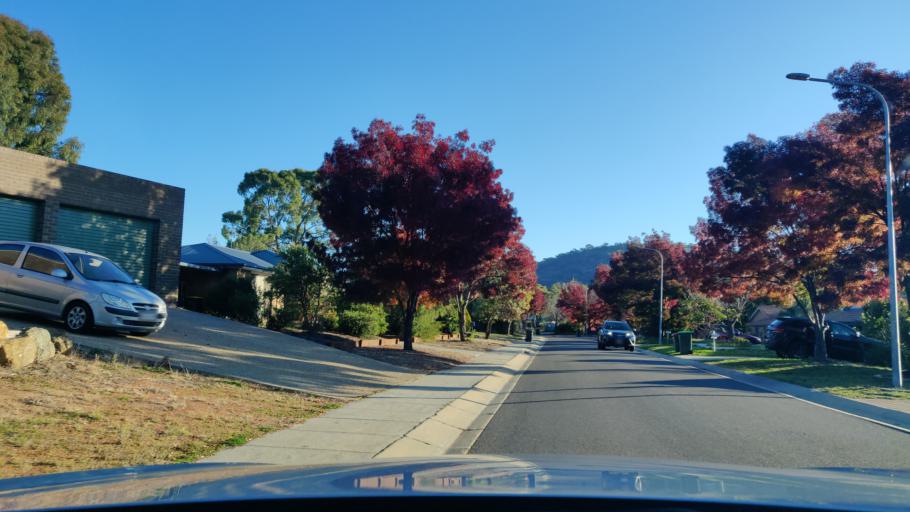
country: AU
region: Australian Capital Territory
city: Macarthur
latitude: -35.4459
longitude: 149.1265
